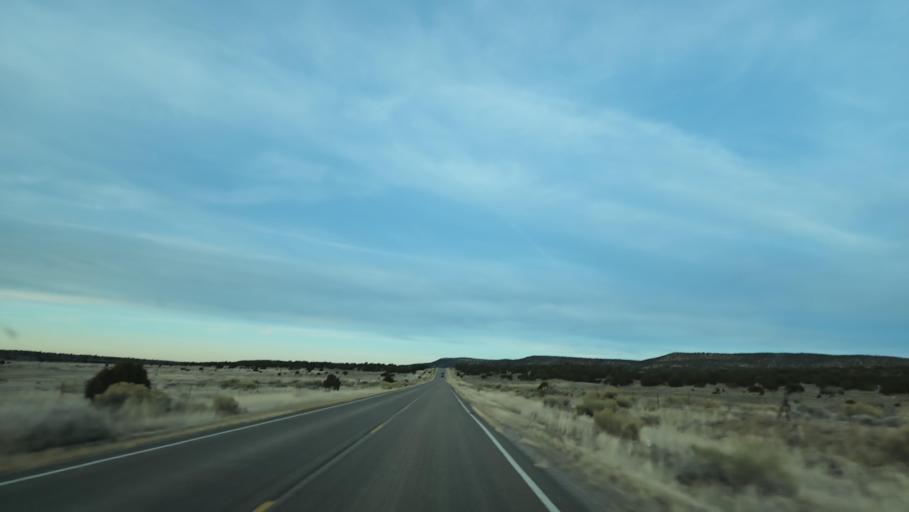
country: US
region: New Mexico
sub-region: Cibola County
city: Grants
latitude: 34.7165
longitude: -107.9839
